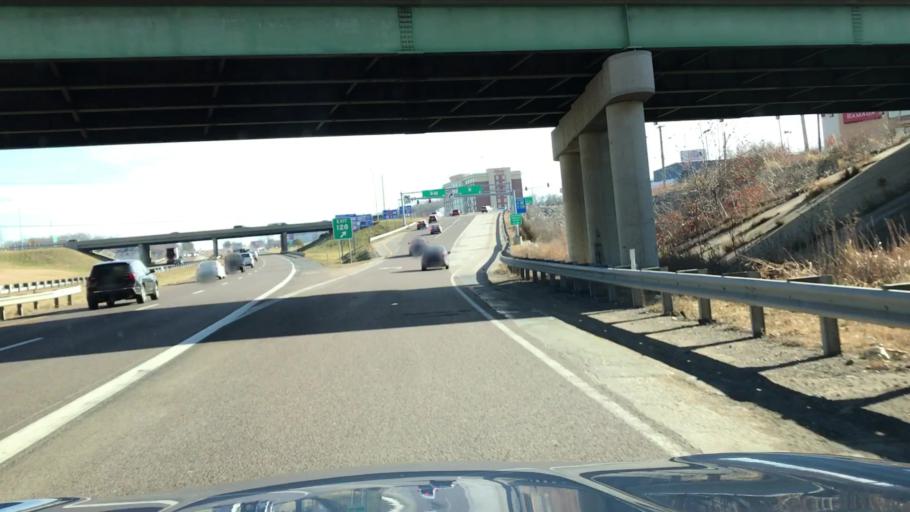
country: US
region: Missouri
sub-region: Boone County
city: Columbia
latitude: 38.9619
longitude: -92.2948
